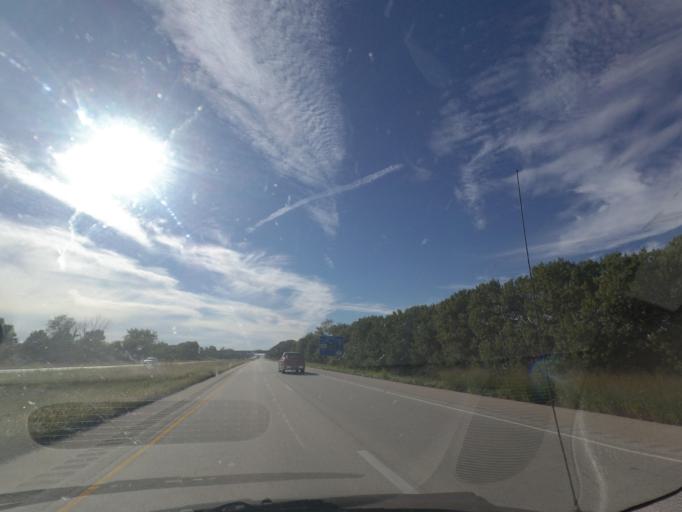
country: US
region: Illinois
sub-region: Macon County
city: Forsyth
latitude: 39.9097
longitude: -88.9145
